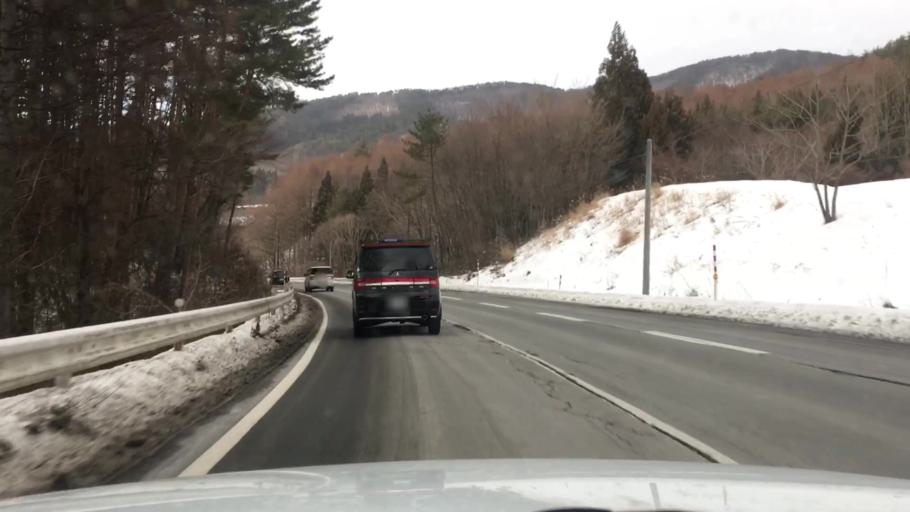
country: JP
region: Iwate
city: Morioka-shi
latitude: 39.6666
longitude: 141.3323
